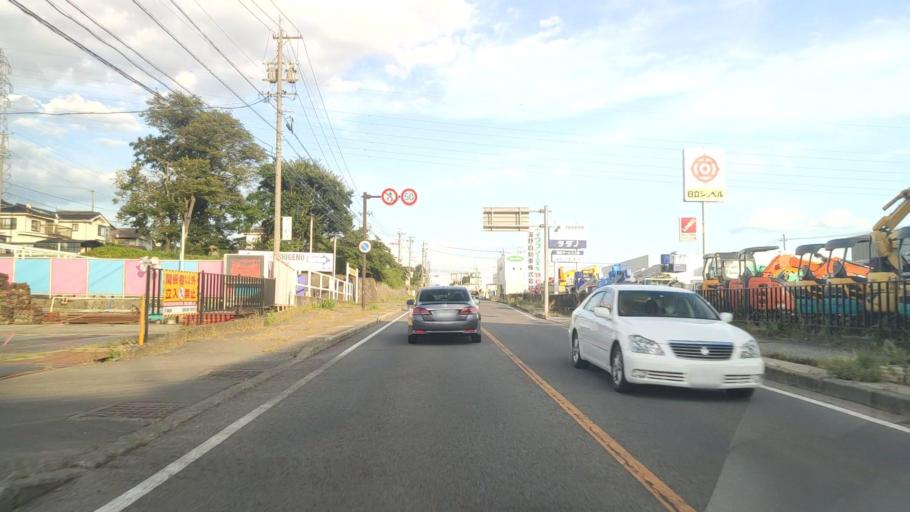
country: JP
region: Nagano
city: Komoro
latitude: 36.3512
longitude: 138.3561
